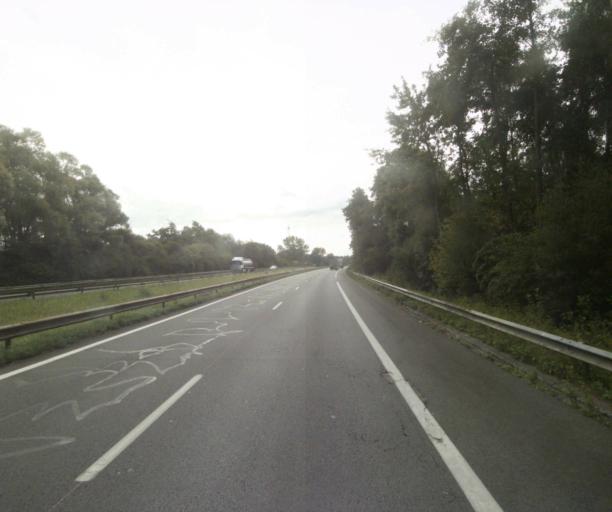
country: FR
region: Nord-Pas-de-Calais
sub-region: Departement du Nord
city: Sainghin-en-Melantois
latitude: 50.5593
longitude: 3.1728
